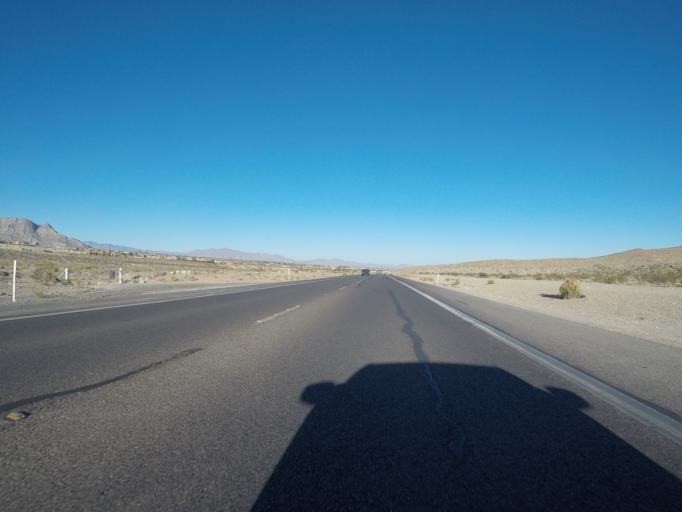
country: US
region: Nevada
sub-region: Clark County
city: Summerlin South
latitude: 36.1504
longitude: -115.3710
